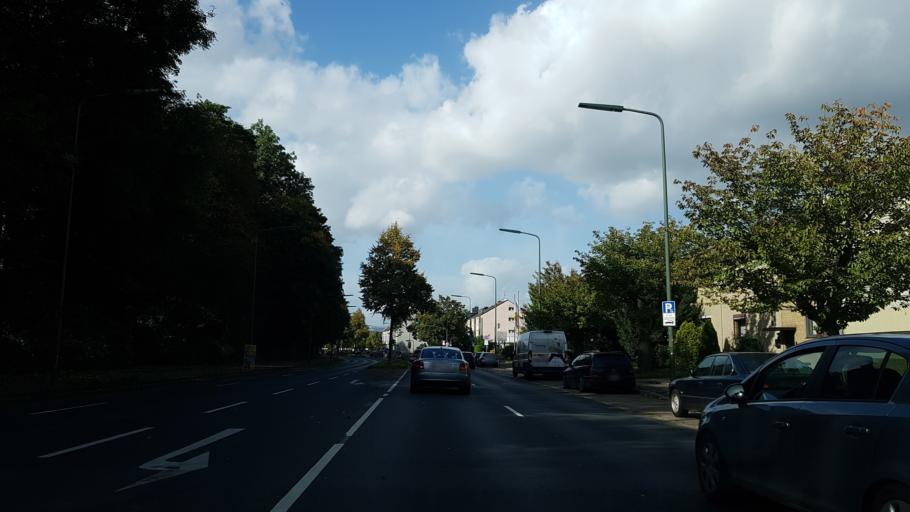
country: DE
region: North Rhine-Westphalia
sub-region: Regierungsbezirk Dusseldorf
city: Erkrath
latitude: 51.1938
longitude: 6.8560
